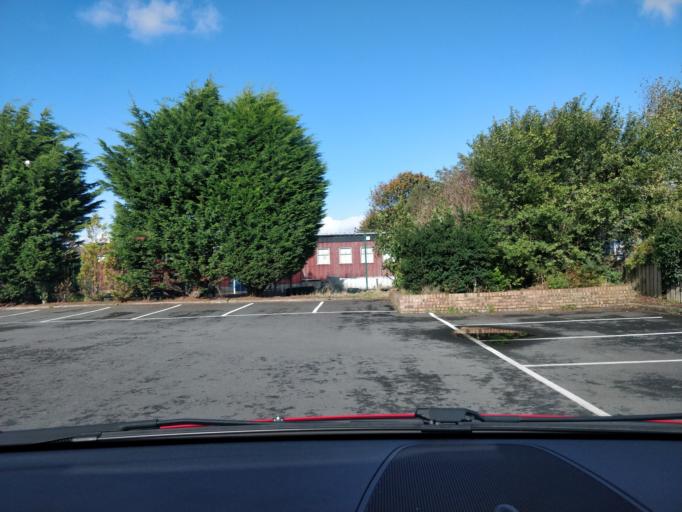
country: GB
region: England
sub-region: Sefton
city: Southport
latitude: 53.6294
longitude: -2.9765
